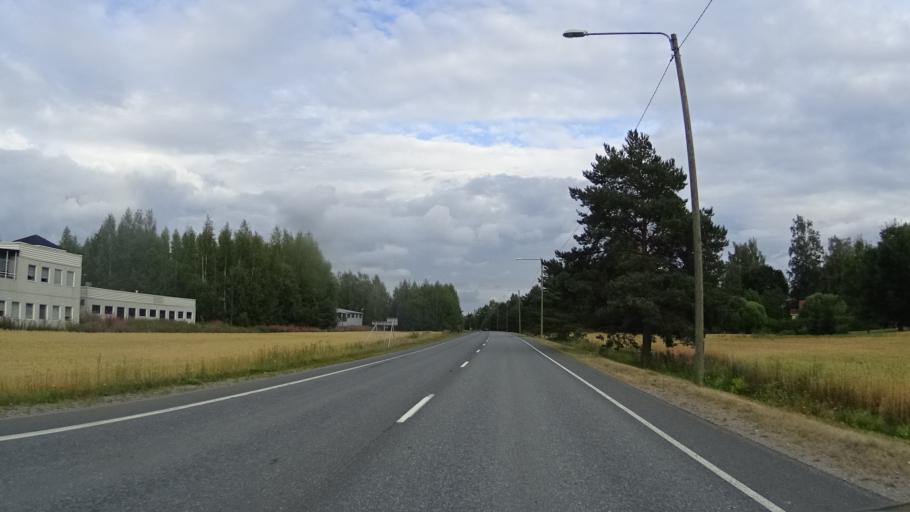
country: FI
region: Haeme
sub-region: Haemeenlinna
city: Parola
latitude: 61.0129
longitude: 24.3919
